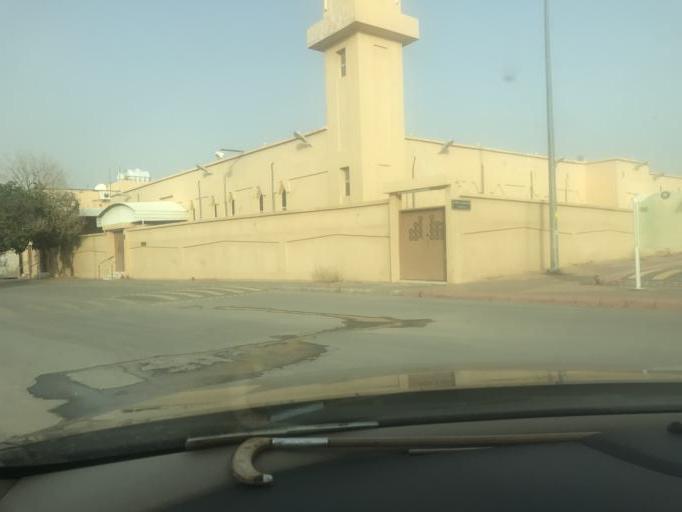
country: SA
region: Ar Riyad
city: Riyadh
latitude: 24.7427
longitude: 46.7728
